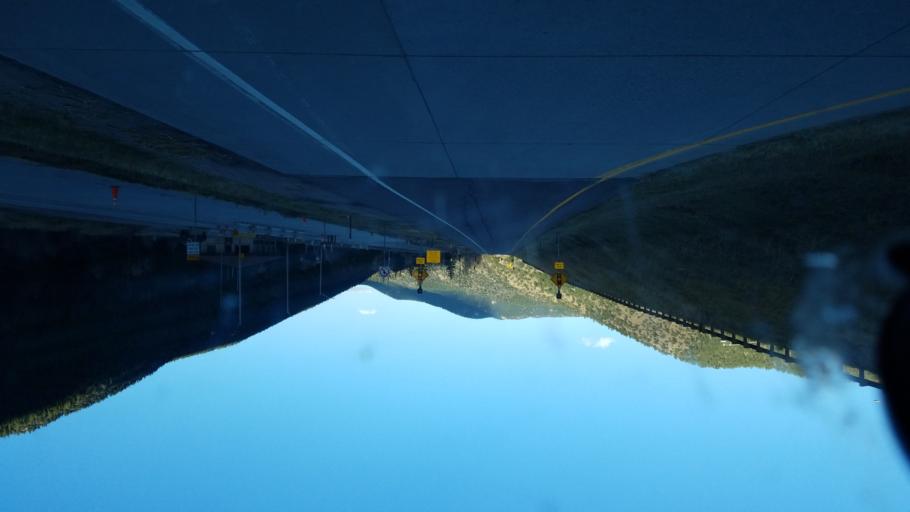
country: US
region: Colorado
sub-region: Clear Creek County
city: Georgetown
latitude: 39.7651
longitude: -105.6137
